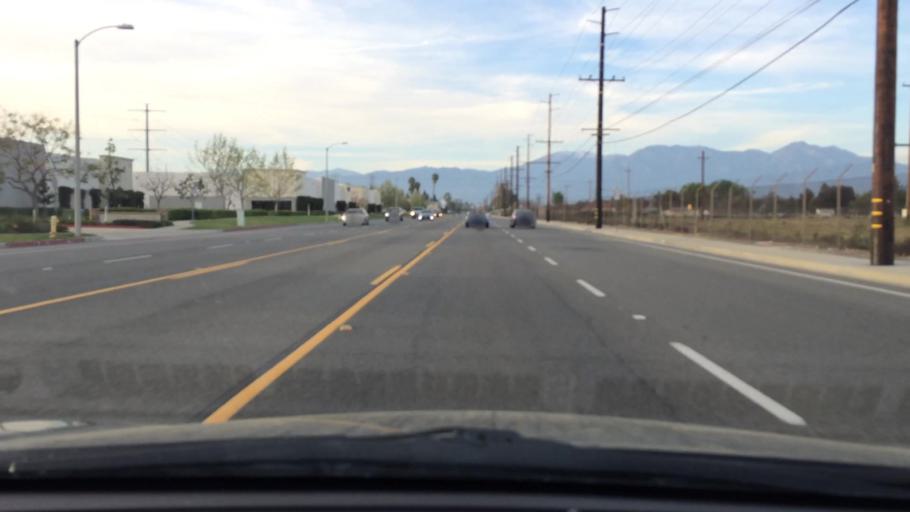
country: US
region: California
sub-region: San Bernardino County
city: Los Serranos
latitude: 33.9860
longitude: -117.6890
